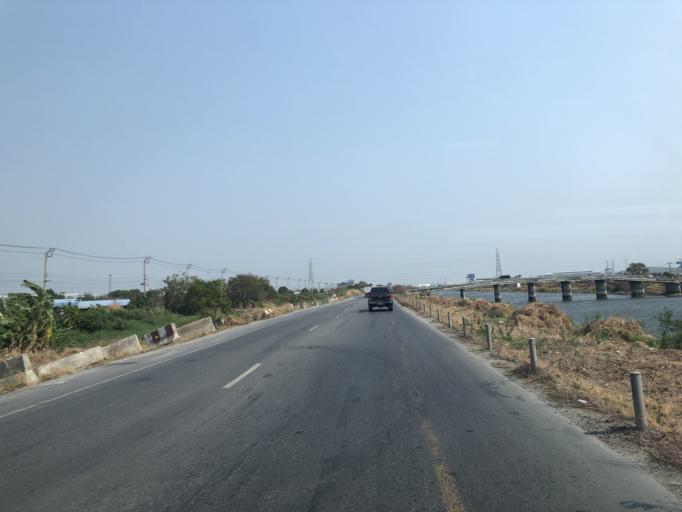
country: TH
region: Samut Prakan
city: Bang Bo District
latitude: 13.5725
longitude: 100.7565
